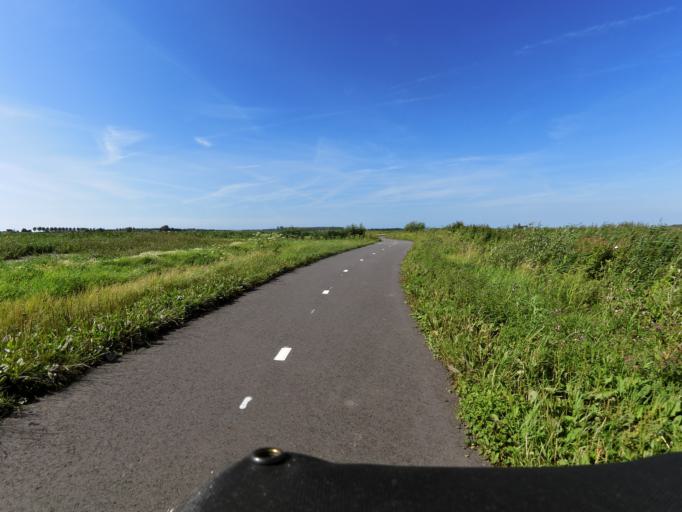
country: NL
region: South Holland
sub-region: Gemeente Goeree-Overflakkee
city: Dirksland
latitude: 51.7457
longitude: 4.0759
